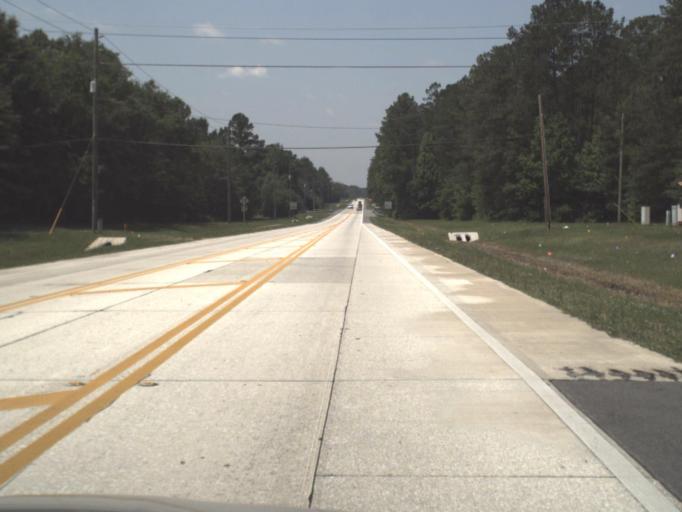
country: US
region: Florida
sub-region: Duval County
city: Baldwin
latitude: 30.2309
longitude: -81.9183
